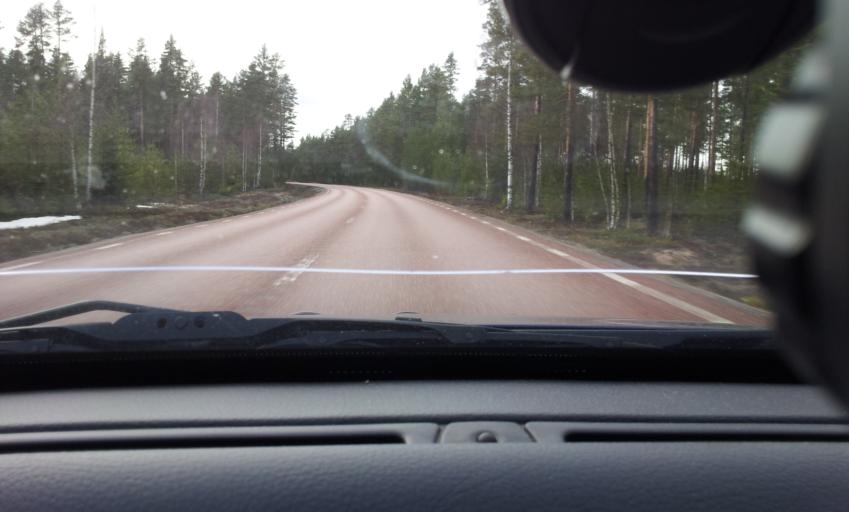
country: SE
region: Gaevleborg
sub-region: Ljusdals Kommun
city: Farila
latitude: 61.8984
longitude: 15.6509
